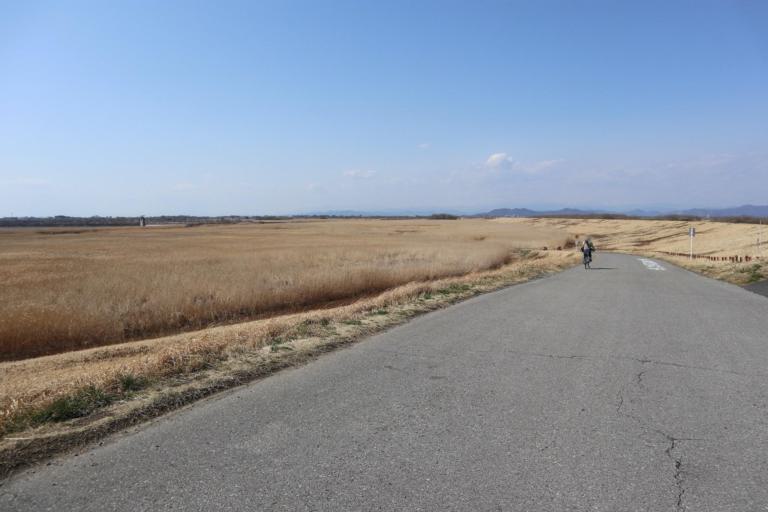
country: JP
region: Ibaraki
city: Koga
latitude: 36.2208
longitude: 139.6943
